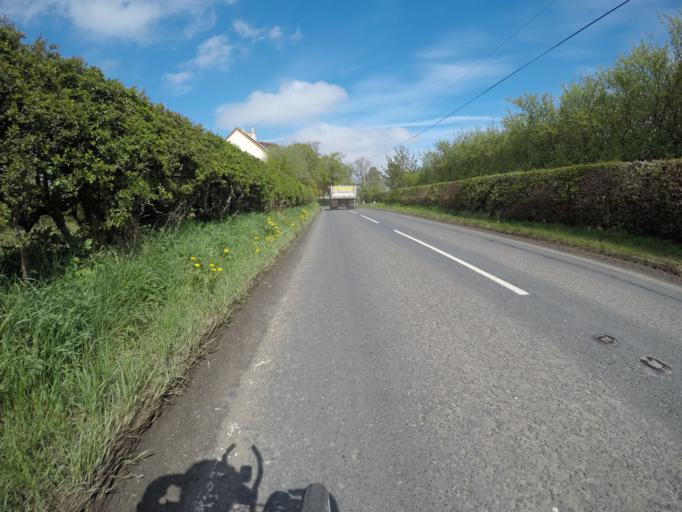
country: GB
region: Scotland
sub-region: East Ayrshire
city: Stewarton
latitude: 55.6930
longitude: -4.4922
